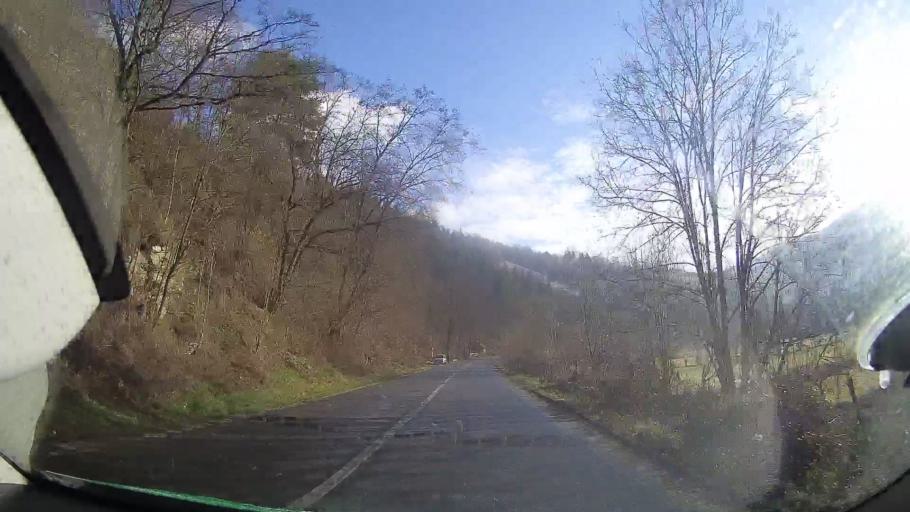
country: RO
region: Alba
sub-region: Comuna Vadu Motilor
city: Vadu Motilor
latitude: 46.3934
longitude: 22.9724
